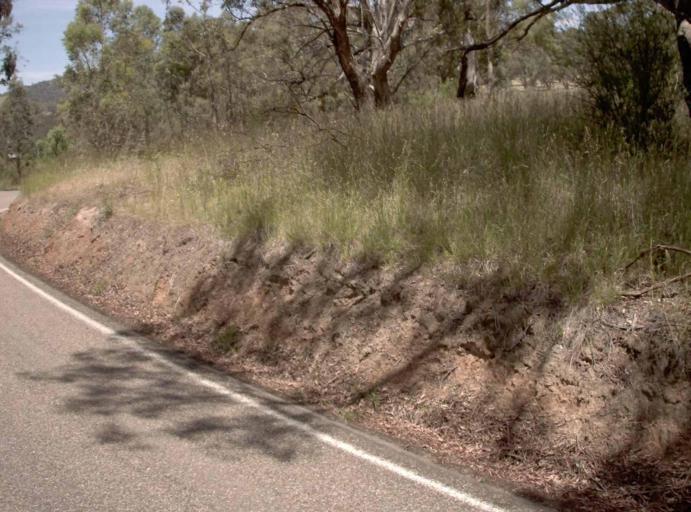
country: AU
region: Victoria
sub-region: East Gippsland
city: Bairnsdale
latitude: -37.3920
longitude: 147.8363
